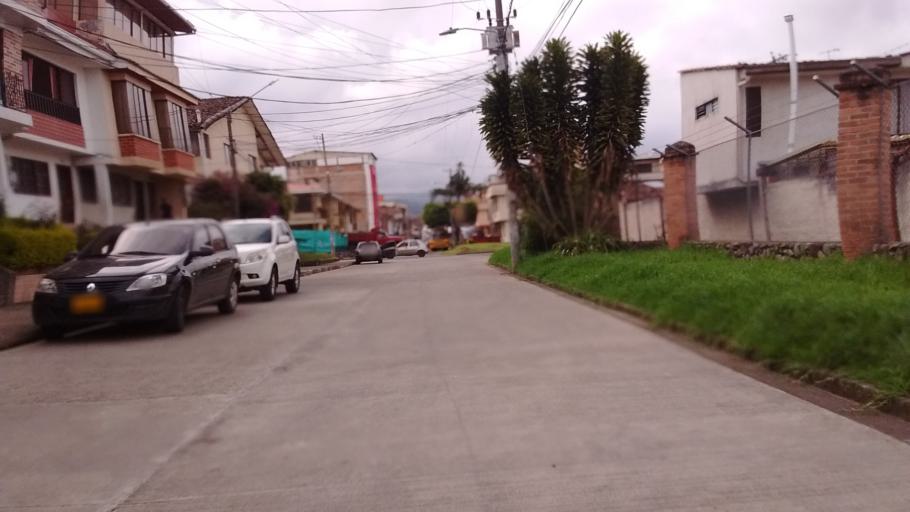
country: CO
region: Cauca
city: Popayan
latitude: 2.4536
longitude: -76.6061
